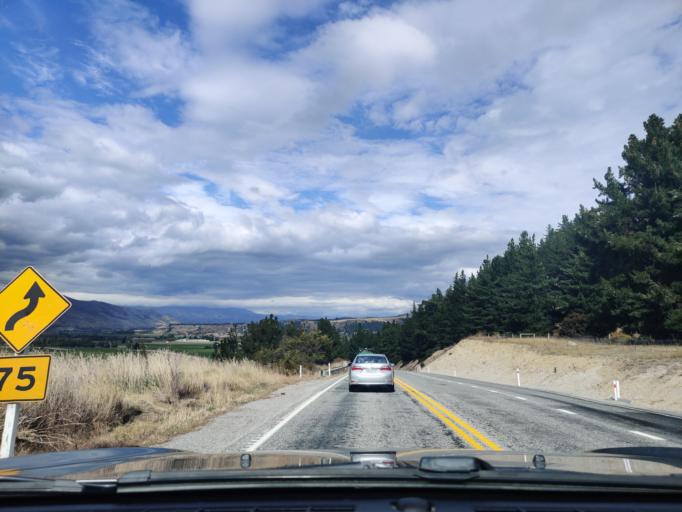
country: NZ
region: Otago
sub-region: Queenstown-Lakes District
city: Wanaka
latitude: -44.7297
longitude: 169.2531
